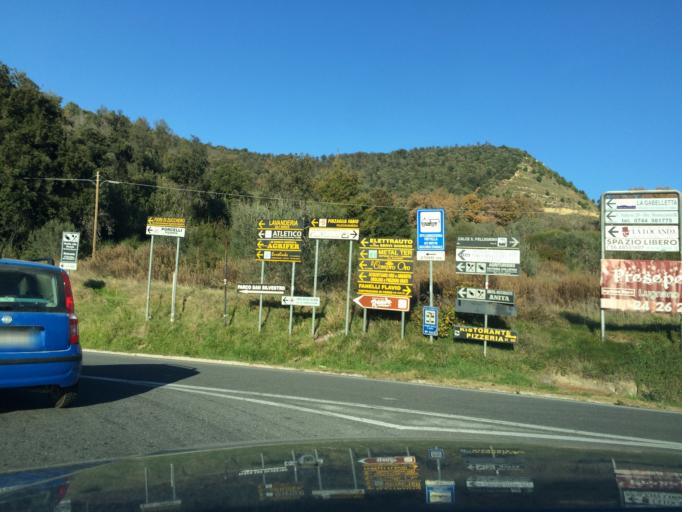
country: IT
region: Umbria
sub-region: Provincia di Terni
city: Fornole
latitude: 42.5385
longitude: 12.4784
